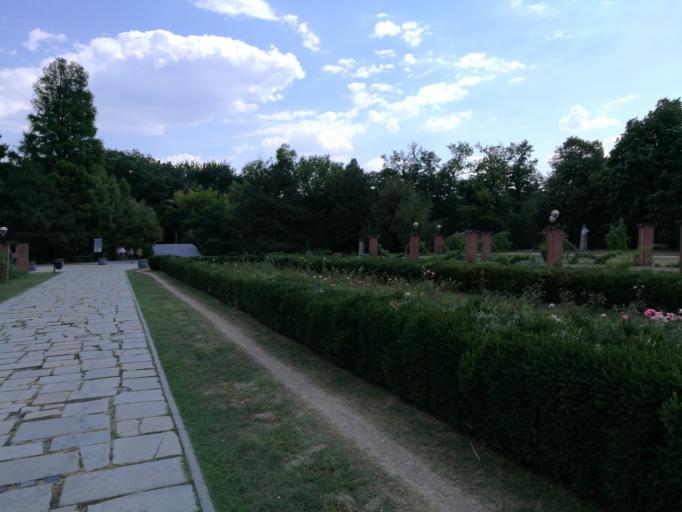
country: RO
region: Bucuresti
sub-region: Municipiul Bucuresti
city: Bucuresti
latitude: 44.4729
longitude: 26.0795
